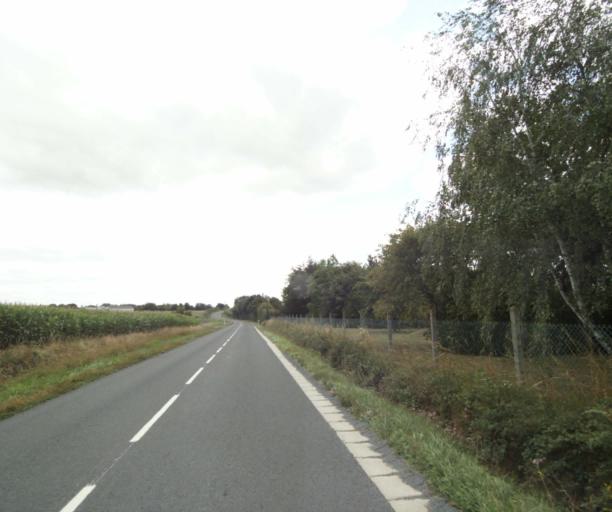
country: FR
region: Pays de la Loire
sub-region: Departement de la Sarthe
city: Sable-sur-Sarthe
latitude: 47.8676
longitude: -0.3377
